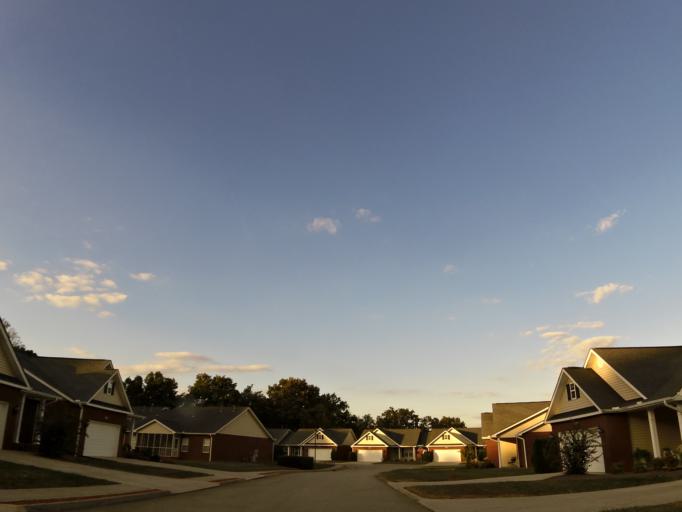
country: US
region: Tennessee
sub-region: Knox County
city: Knoxville
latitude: 36.0509
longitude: -83.9000
